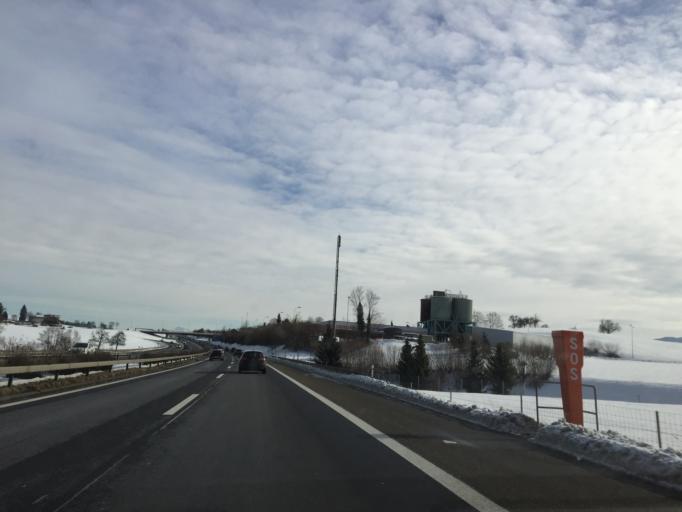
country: CH
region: Zurich
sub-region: Bezirk Horgen
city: Au / Unter-Dorf
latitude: 47.2313
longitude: 8.6259
